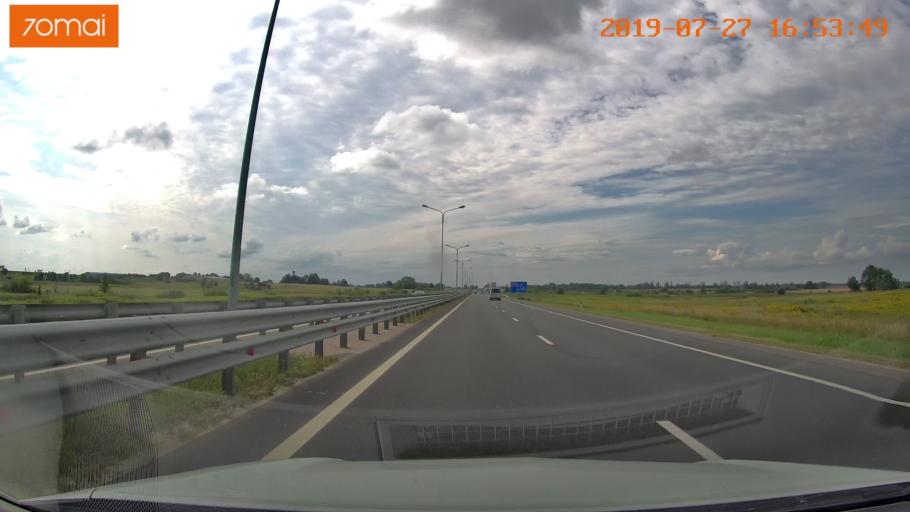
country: RU
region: Kaliningrad
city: Bol'shoe Isakovo
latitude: 54.6904
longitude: 20.8238
